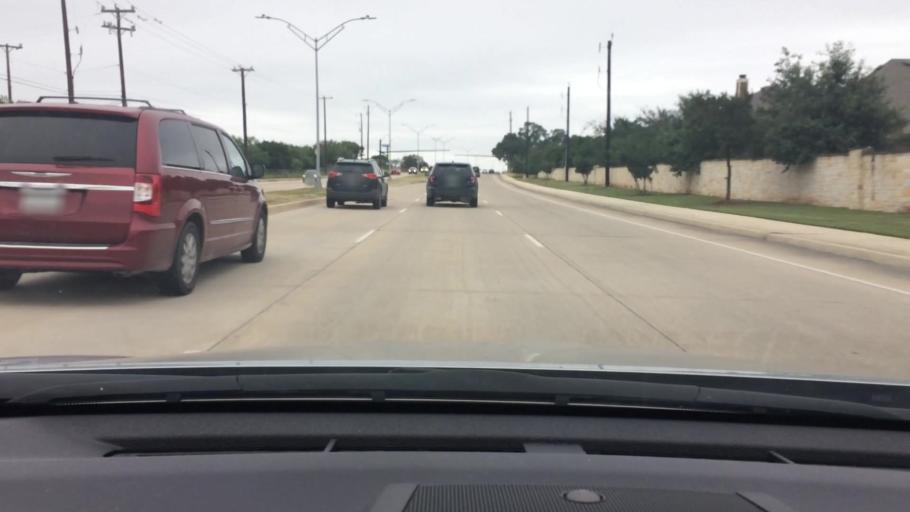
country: US
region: Texas
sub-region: Bexar County
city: Hollywood Park
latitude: 29.6140
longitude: -98.4214
